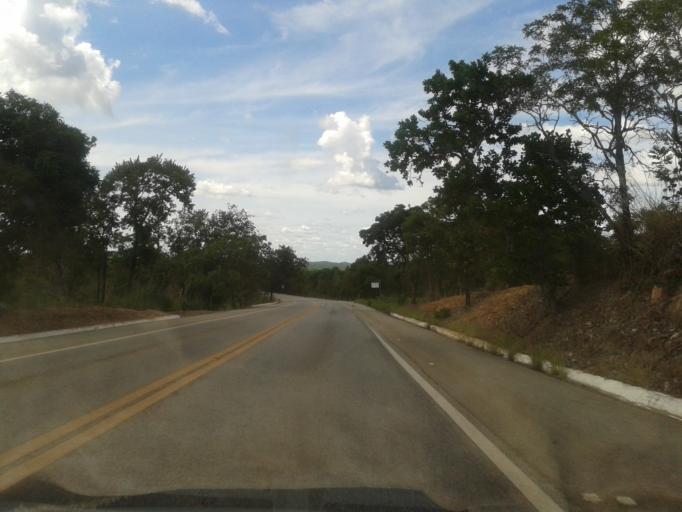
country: BR
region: Goias
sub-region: Itapuranga
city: Itapuranga
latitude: -15.5047
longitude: -50.3037
